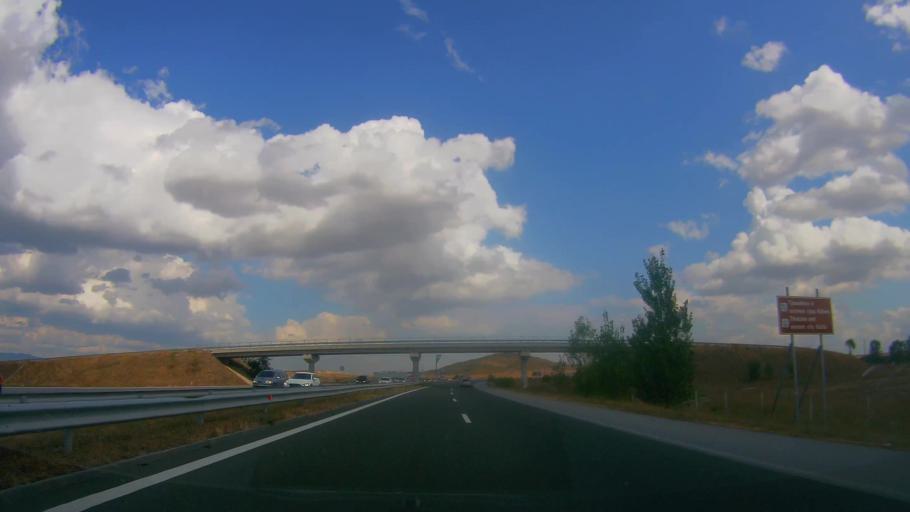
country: BG
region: Yambol
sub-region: Obshtina Yambol
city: Yambol
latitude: 42.5443
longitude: 26.4435
